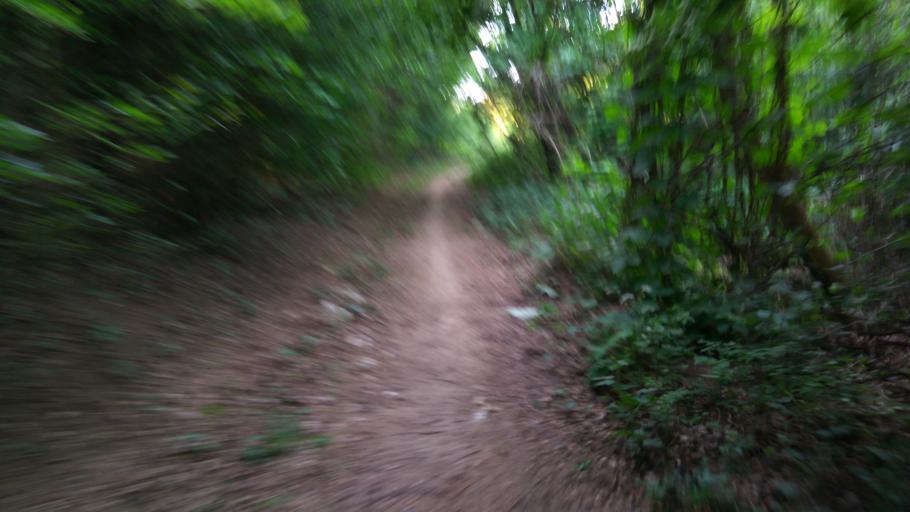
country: HU
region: Pest
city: Csobanka
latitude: 47.6516
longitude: 18.9850
